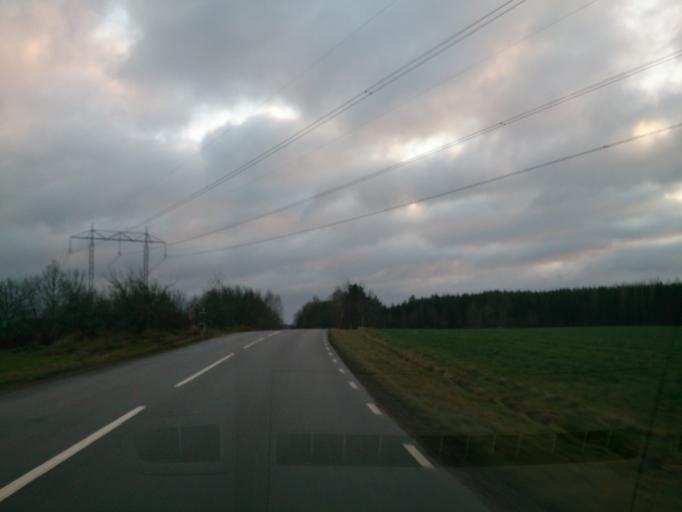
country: SE
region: OEstergoetland
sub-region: Atvidabergs Kommun
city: Atvidaberg
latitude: 58.3711
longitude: 16.0244
